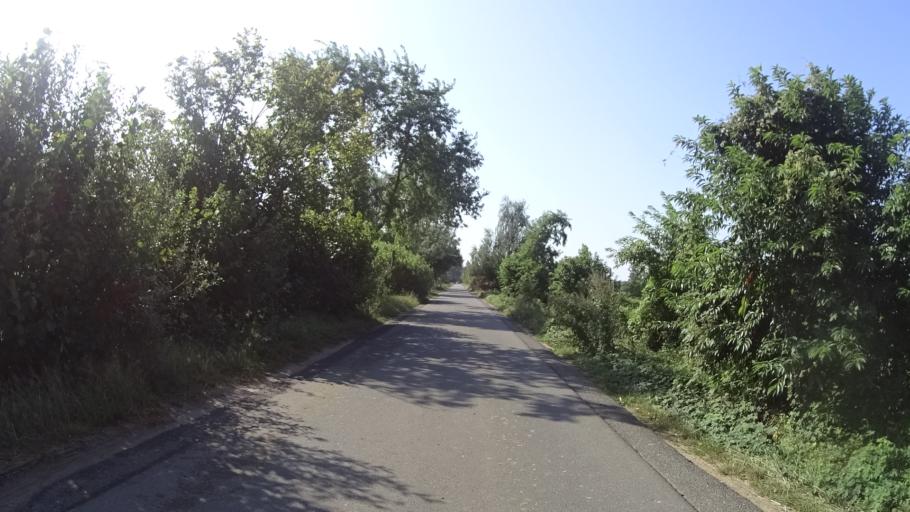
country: DE
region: Brandenburg
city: Straupitz
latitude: 51.8936
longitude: 14.1250
